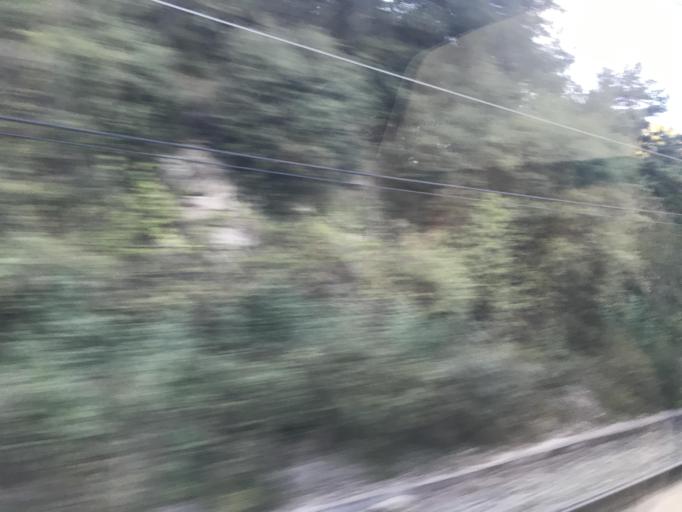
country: ES
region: Basque Country
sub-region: Provincia de Alava
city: Arminon
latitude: 42.7338
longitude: -2.8751
